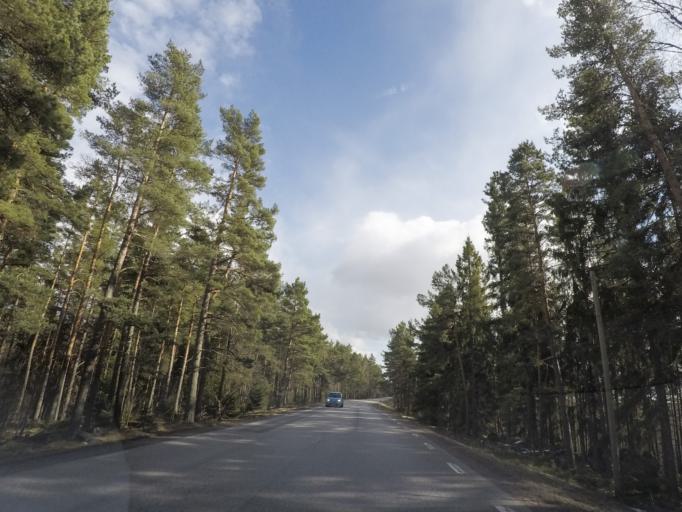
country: SE
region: Vaestmanland
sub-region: Hallstahammars Kommun
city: Hallstahammar
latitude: 59.6485
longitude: 16.1889
